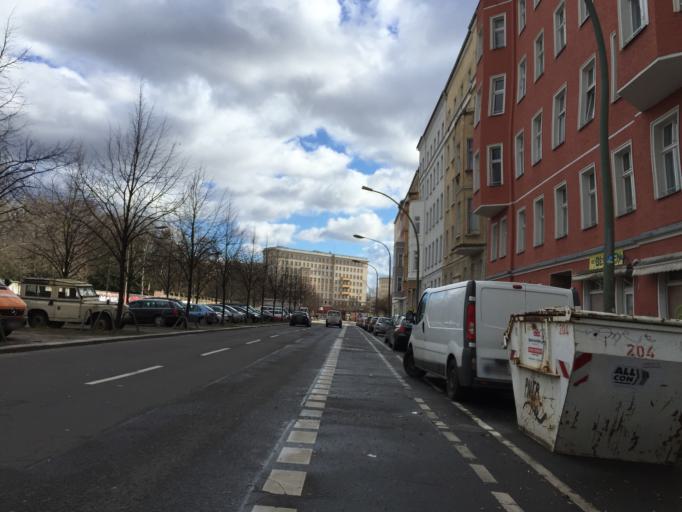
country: DE
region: Berlin
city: Friedrichshain Bezirk
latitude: 52.5195
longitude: 13.4390
